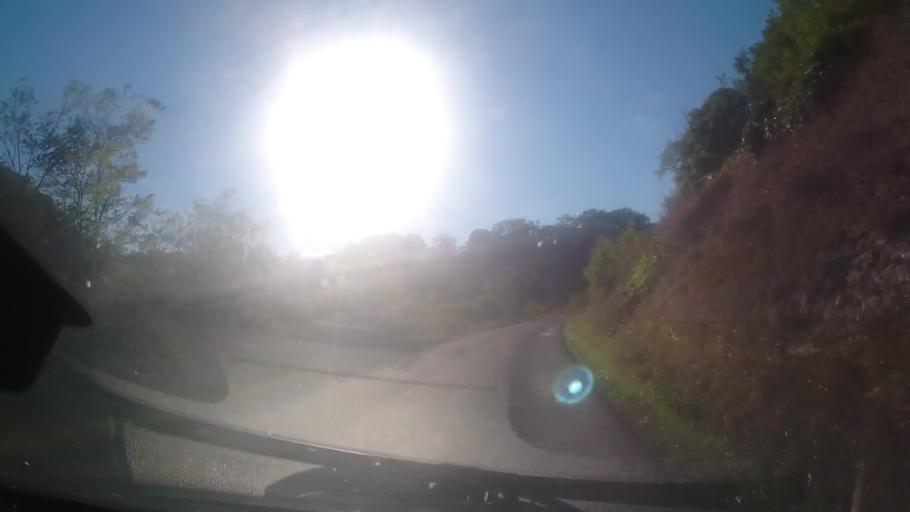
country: FR
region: Aquitaine
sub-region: Departement de la Dordogne
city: Cenac-et-Saint-Julien
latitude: 44.7974
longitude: 1.1937
